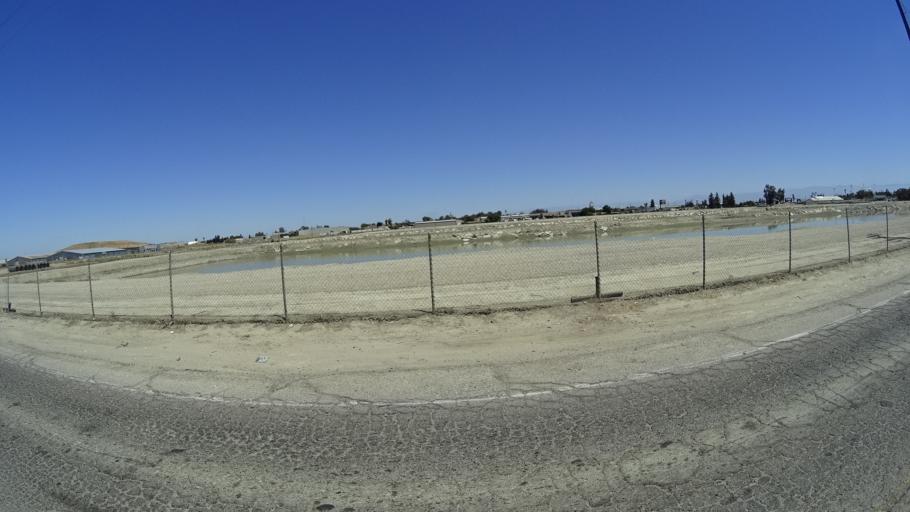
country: US
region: California
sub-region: Fresno County
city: Easton
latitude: 36.6777
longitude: -119.7499
